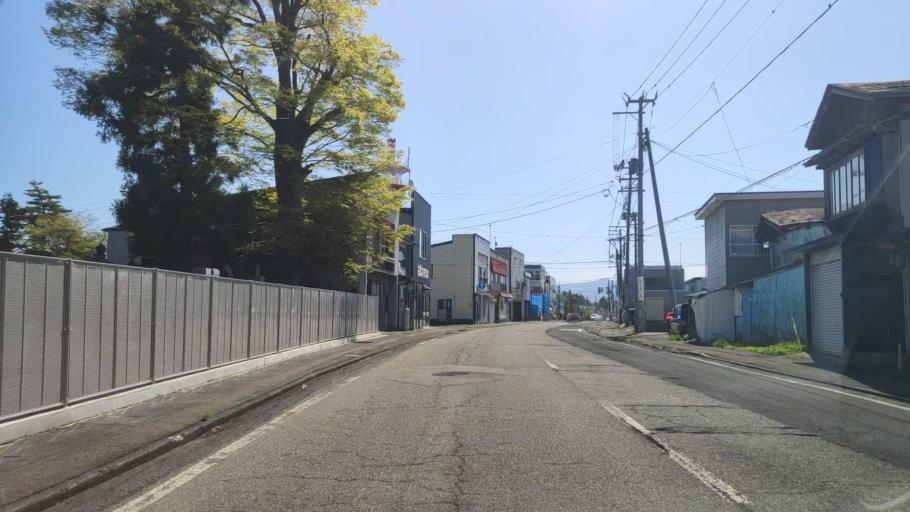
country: JP
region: Akita
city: Omagari
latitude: 39.4588
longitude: 140.4764
